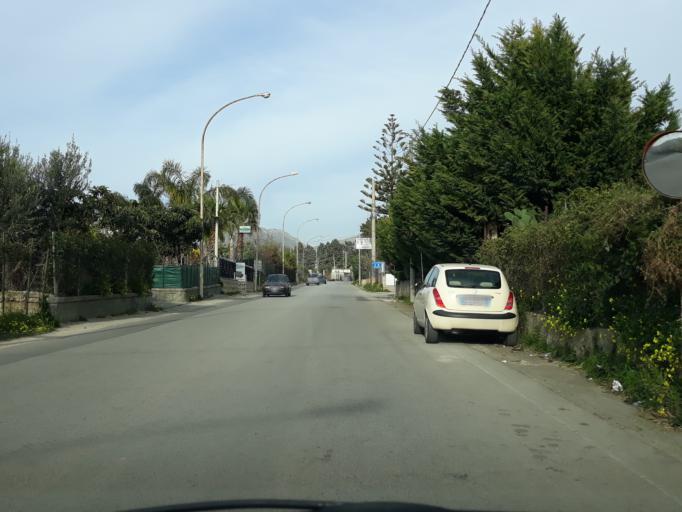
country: IT
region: Sicily
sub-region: Palermo
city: Borgetto
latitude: 38.0592
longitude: 13.1359
